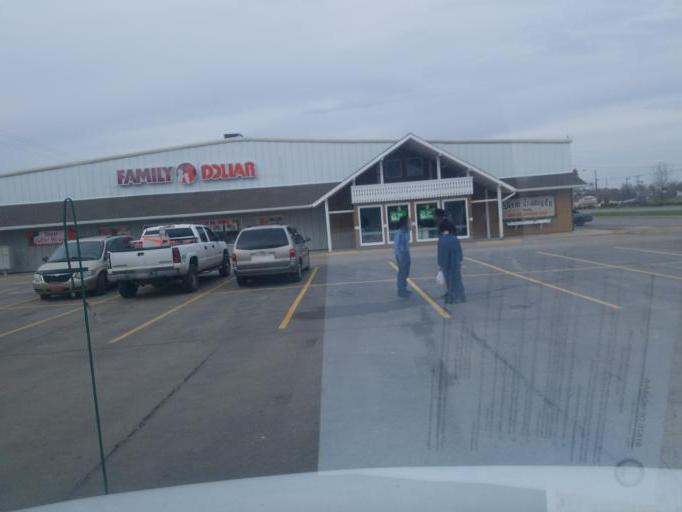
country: US
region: Indiana
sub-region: Adams County
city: Berne
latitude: 40.6673
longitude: -84.9560
